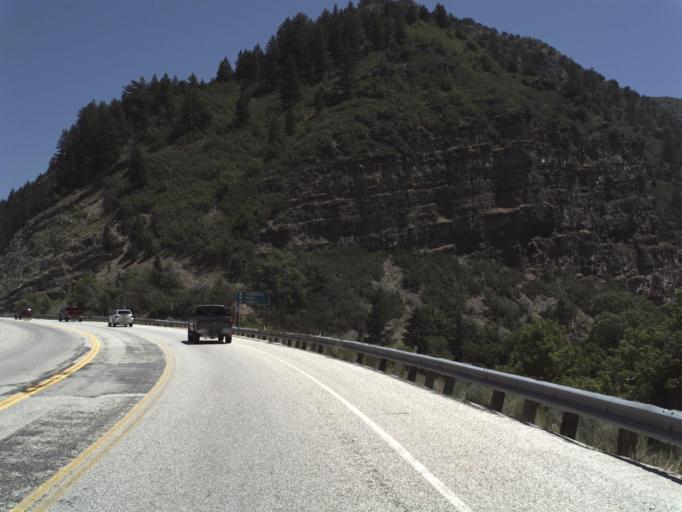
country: US
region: Utah
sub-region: Weber County
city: Liberty
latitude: 41.2540
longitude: -111.8468
